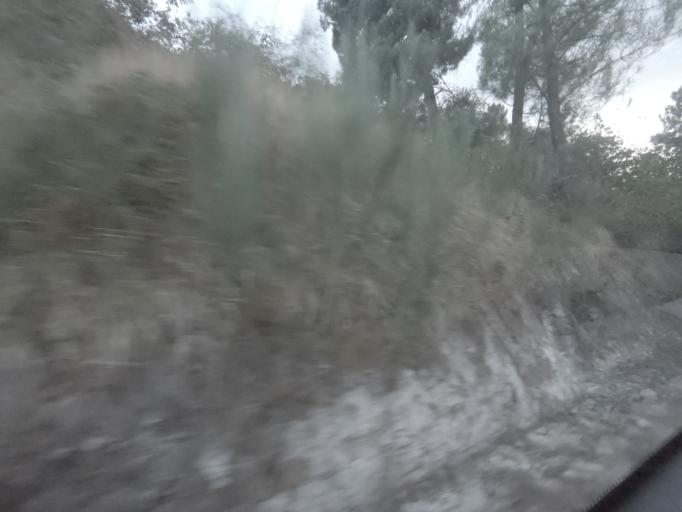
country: PT
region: Viseu
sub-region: Armamar
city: Armamar
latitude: 41.1279
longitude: -7.7365
